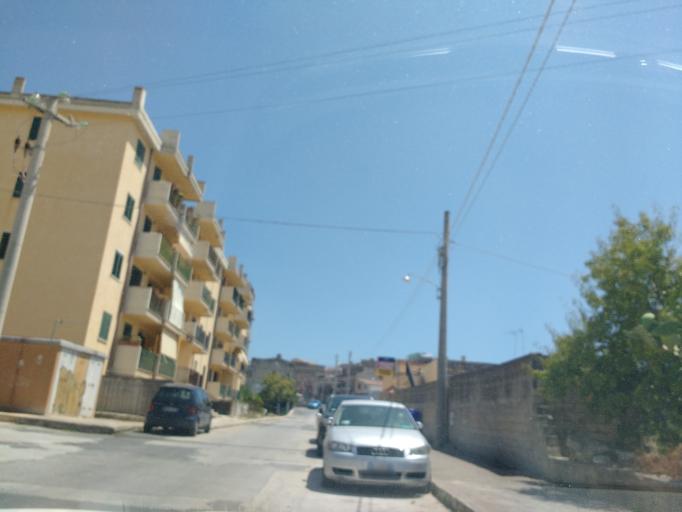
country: IT
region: Sicily
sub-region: Provincia di Siracusa
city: Noto
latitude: 36.8905
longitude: 15.0613
